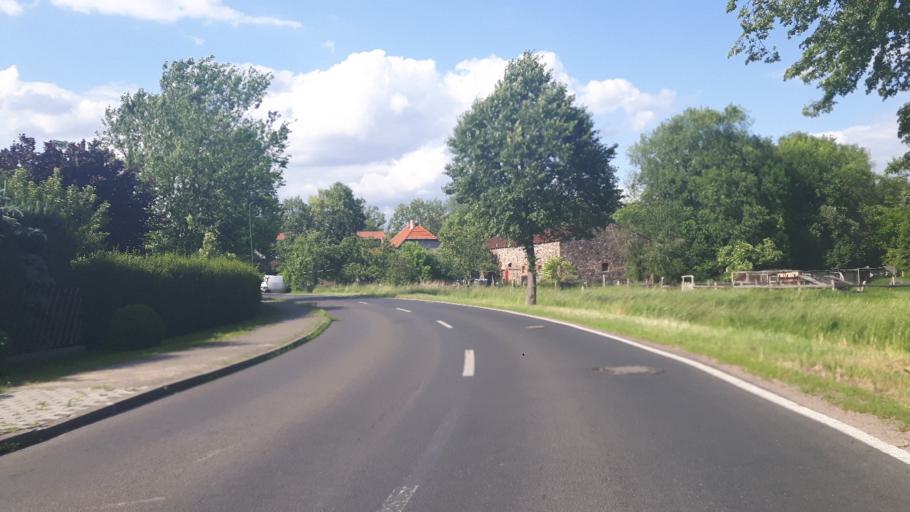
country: DE
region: Brandenburg
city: Melchow
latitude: 52.7373
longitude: 13.7112
